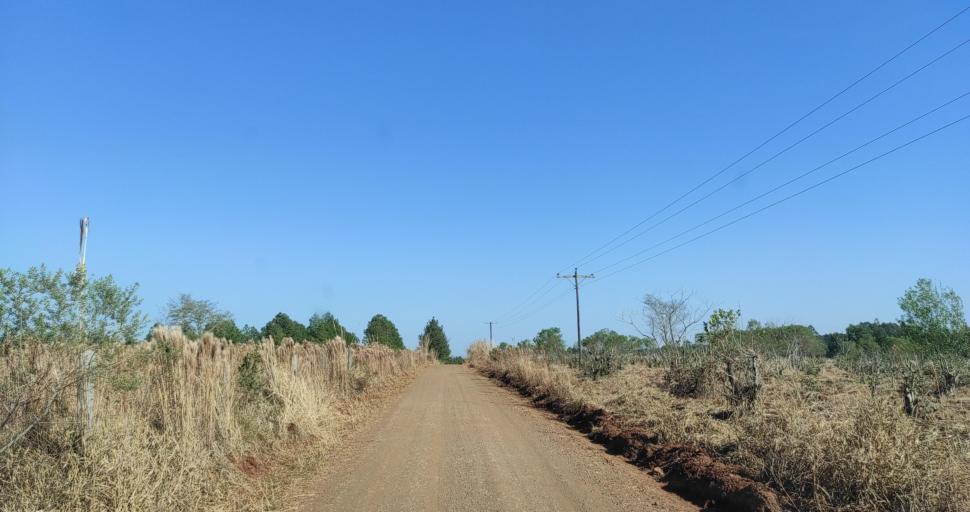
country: AR
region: Misiones
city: Capiovi
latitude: -26.8937
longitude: -55.0451
